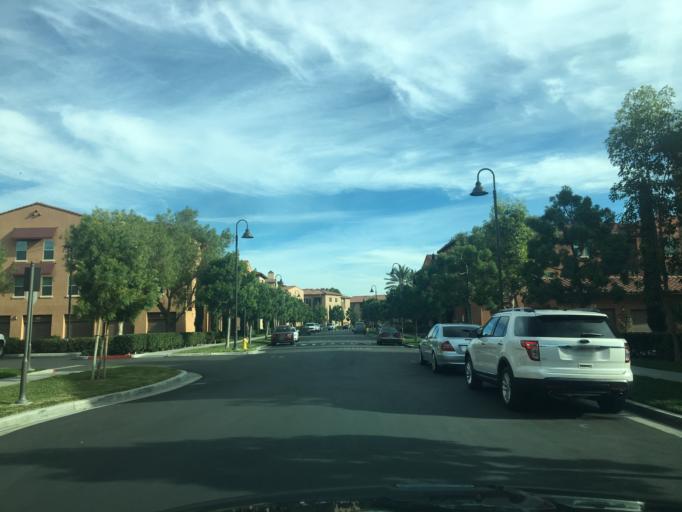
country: US
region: California
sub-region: Orange County
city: Laguna Woods
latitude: 33.6478
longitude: -117.7509
